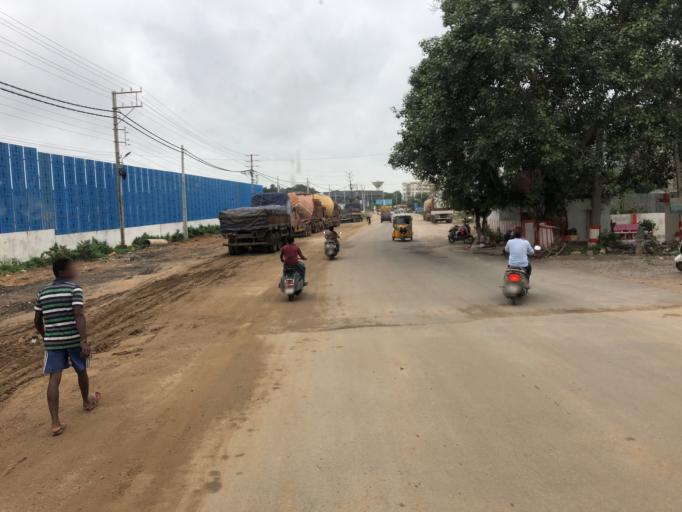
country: IN
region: Telangana
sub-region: Medak
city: Serilingampalle
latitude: 17.4664
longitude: 78.3382
